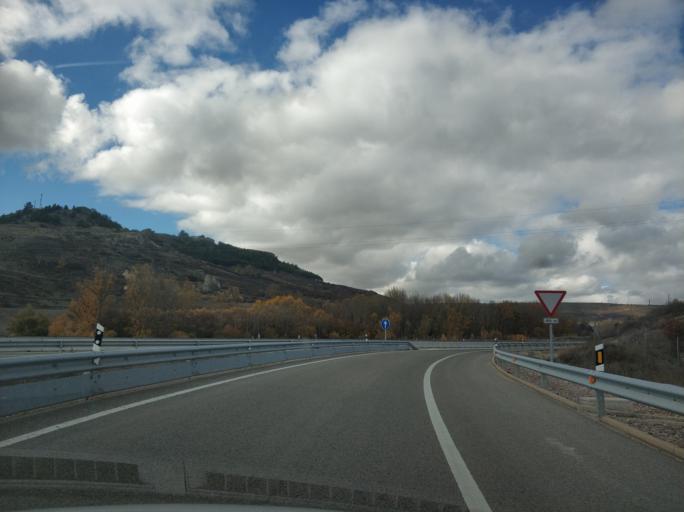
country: ES
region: Castille and Leon
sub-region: Provincia de Soria
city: Medinaceli
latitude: 41.1724
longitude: -2.4202
